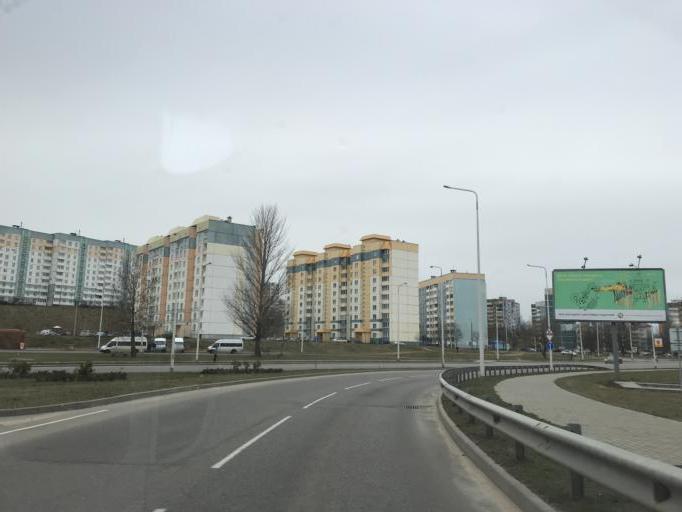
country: BY
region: Mogilev
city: Mahilyow
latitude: 53.8826
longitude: 30.3789
